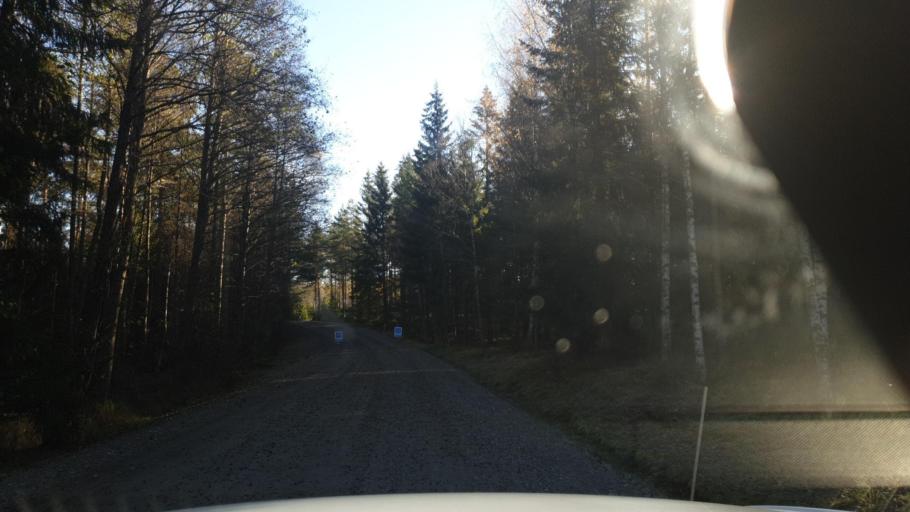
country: SE
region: Vaermland
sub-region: Karlstads Kommun
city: Valberg
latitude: 59.4166
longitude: 13.1460
